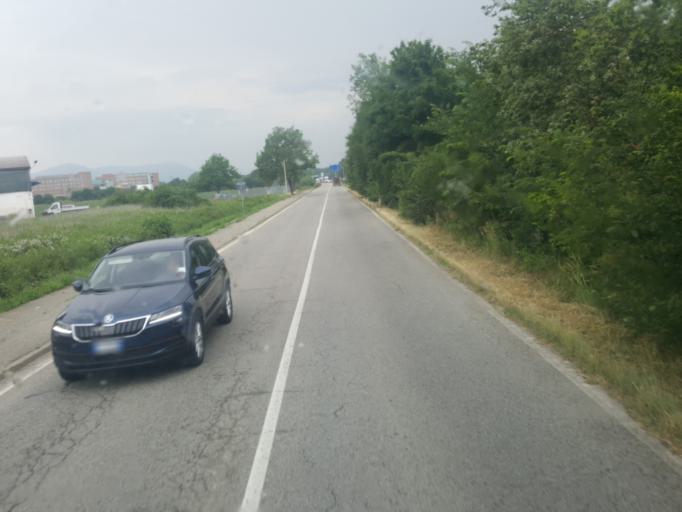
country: IT
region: Piedmont
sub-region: Provincia di Torino
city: Candiolo
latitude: 44.9632
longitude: 7.5755
